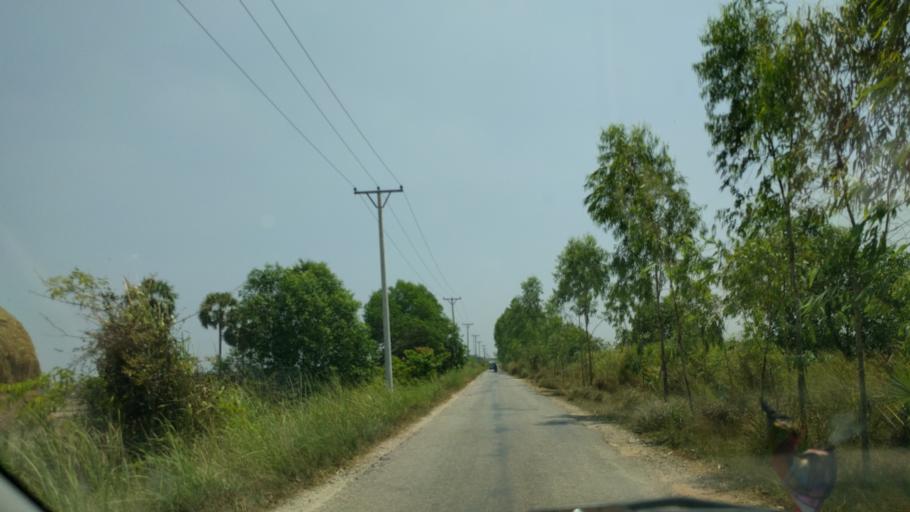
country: MM
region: Mon
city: Martaban
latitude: 16.5861
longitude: 97.6749
